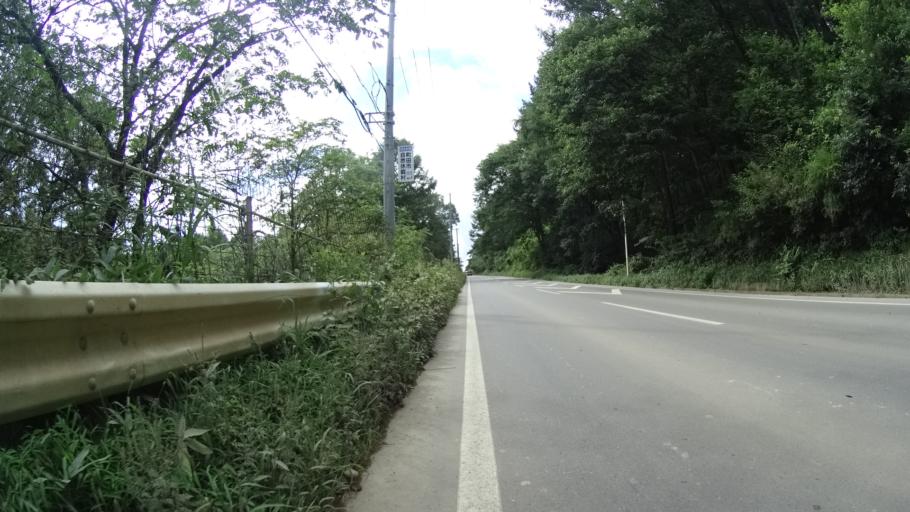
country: JP
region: Nagano
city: Saku
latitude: 35.9639
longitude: 138.5361
